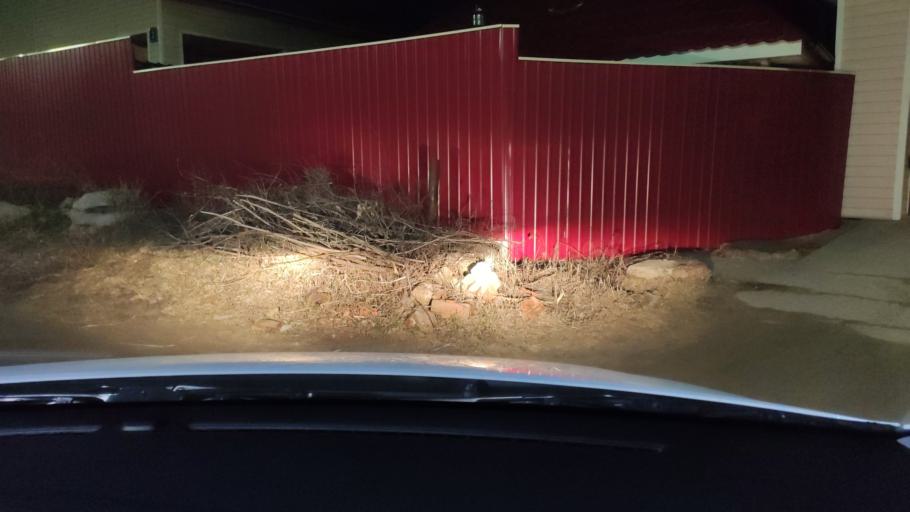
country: RU
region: Tatarstan
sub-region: Gorod Kazan'
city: Kazan
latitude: 55.8450
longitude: 49.2109
